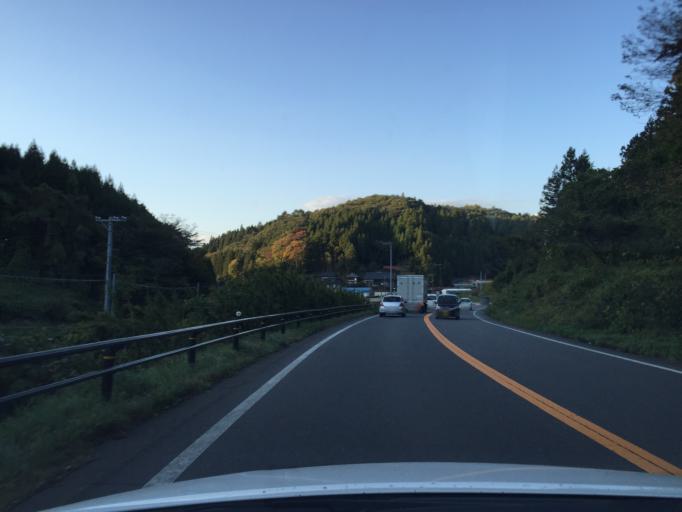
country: JP
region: Fukushima
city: Miharu
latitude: 37.2880
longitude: 140.5428
